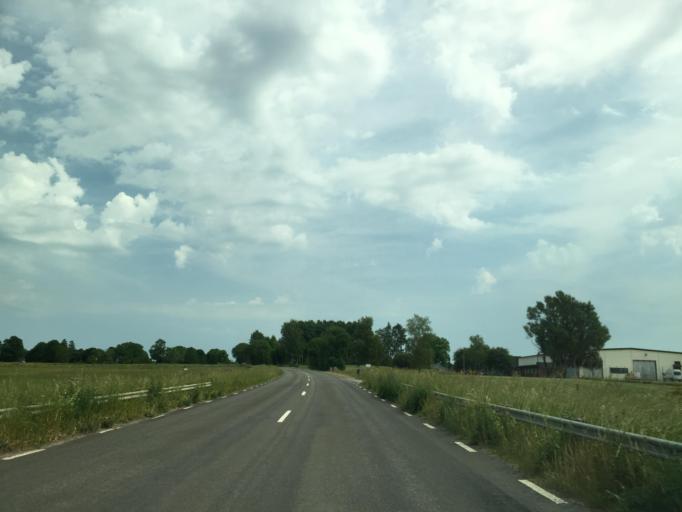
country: SE
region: Vaestra Goetaland
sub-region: Skovde Kommun
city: Skultorp
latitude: 58.3309
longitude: 13.7815
